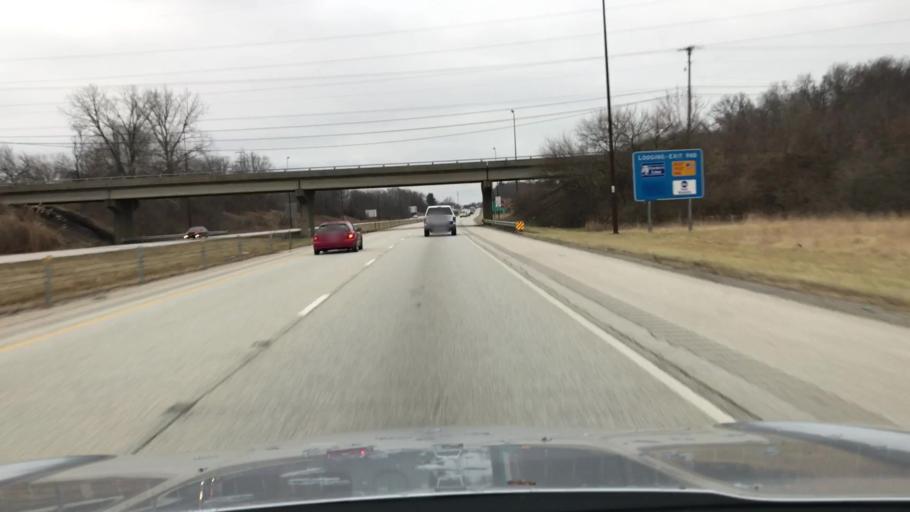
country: US
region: Illinois
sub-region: Sangamon County
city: Grandview
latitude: 39.8250
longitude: -89.5927
